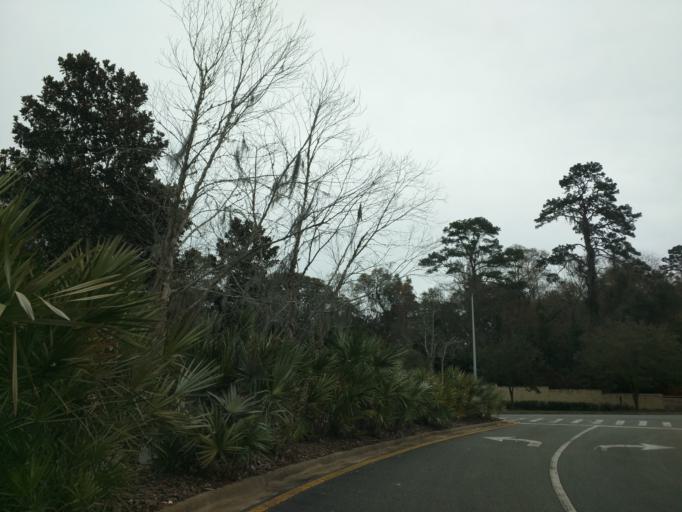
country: US
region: Florida
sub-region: Leon County
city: Tallahassee
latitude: 30.4497
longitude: -84.2513
